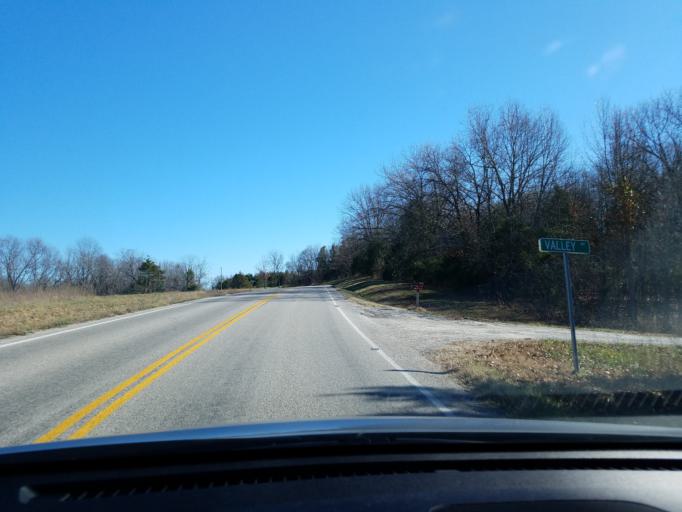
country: US
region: Missouri
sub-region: Taney County
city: Hollister
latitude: 36.5258
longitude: -93.2816
